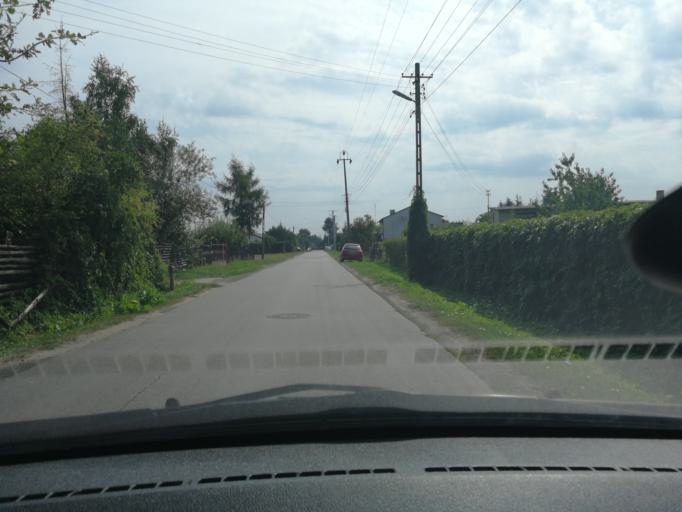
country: PL
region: Lodz Voivodeship
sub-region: Skierniewice
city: Skierniewice
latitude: 51.9708
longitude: 20.1159
